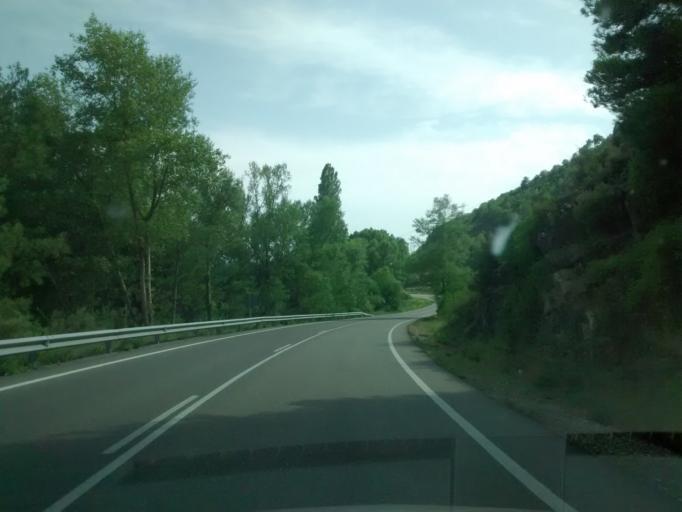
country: ES
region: Aragon
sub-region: Provincia de Huesca
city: Labuerda
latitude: 42.4730
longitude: 0.1468
